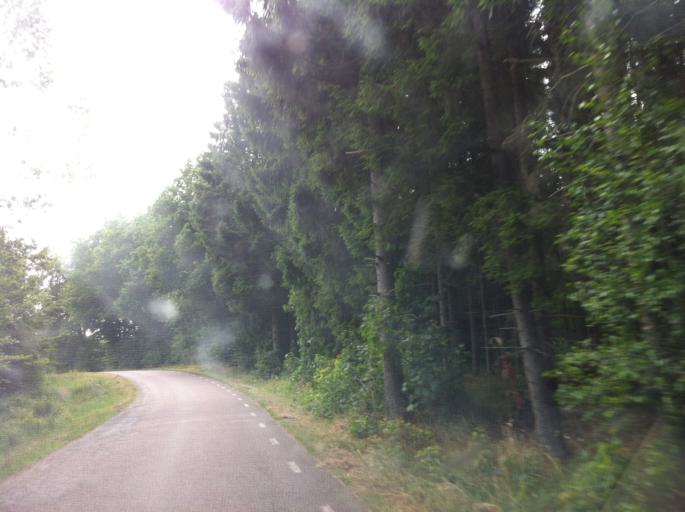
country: SE
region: Skane
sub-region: Eslovs Kommun
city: Eslov
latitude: 55.9282
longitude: 13.2653
